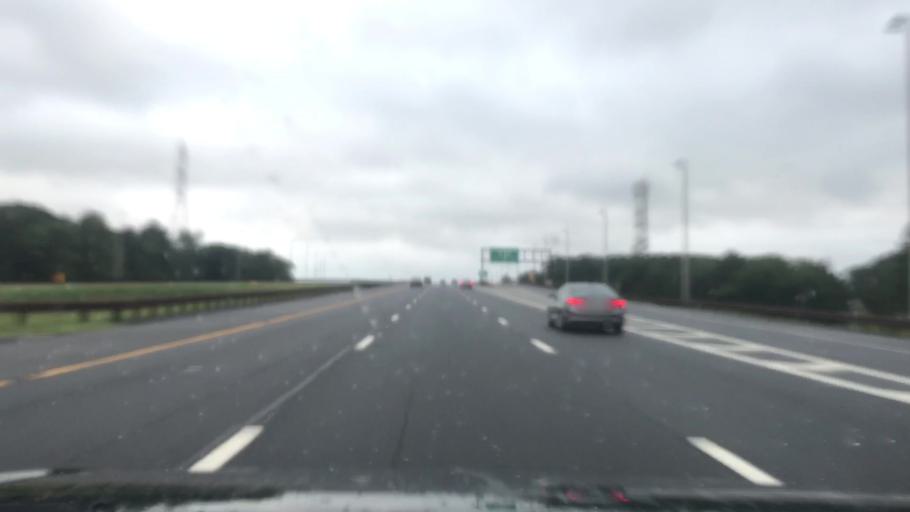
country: US
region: New Jersey
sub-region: Ocean County
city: Silver Ridge
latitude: 39.9848
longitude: -74.2119
